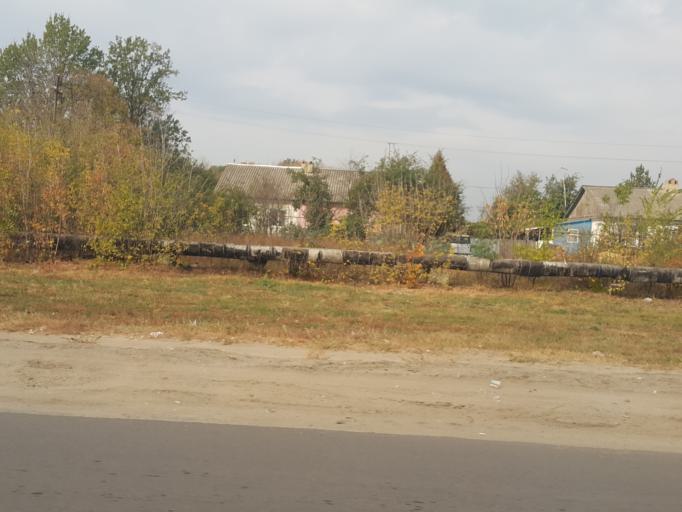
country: RU
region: Tambov
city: Bokino
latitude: 52.6523
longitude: 41.4449
